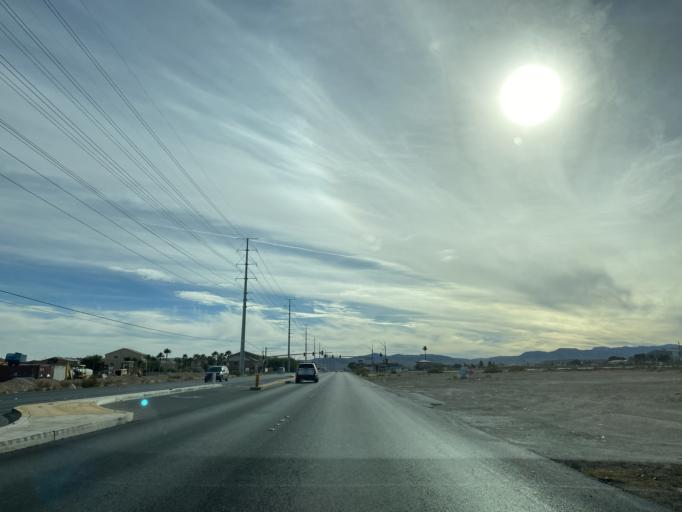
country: US
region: Nevada
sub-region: Clark County
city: Enterprise
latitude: 36.0361
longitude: -115.2436
